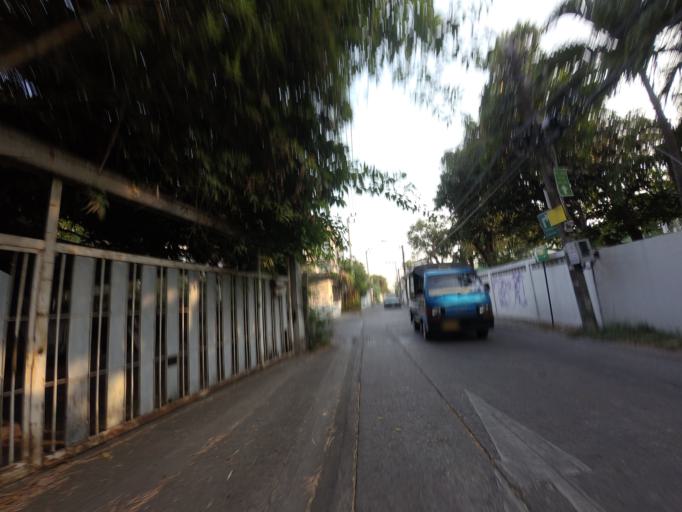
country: TH
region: Bangkok
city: Watthana
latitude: 13.7272
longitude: 100.5911
